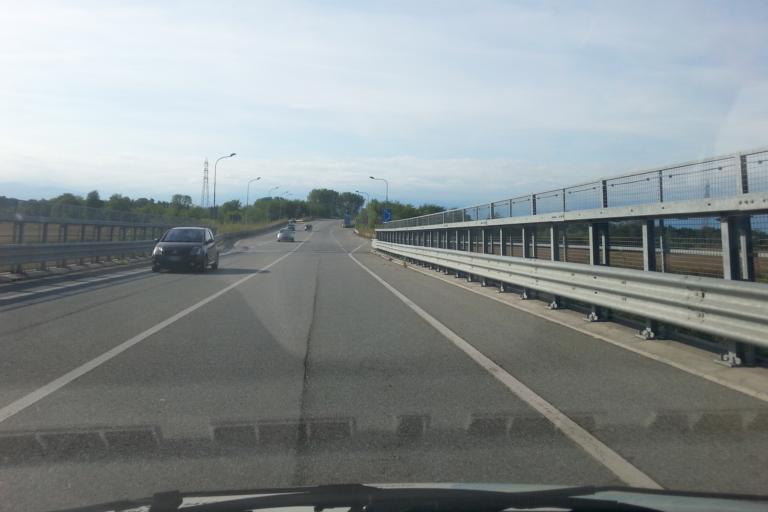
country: IT
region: Piedmont
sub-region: Provincia di Torino
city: Brandizzo
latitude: 45.1587
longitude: 7.8267
